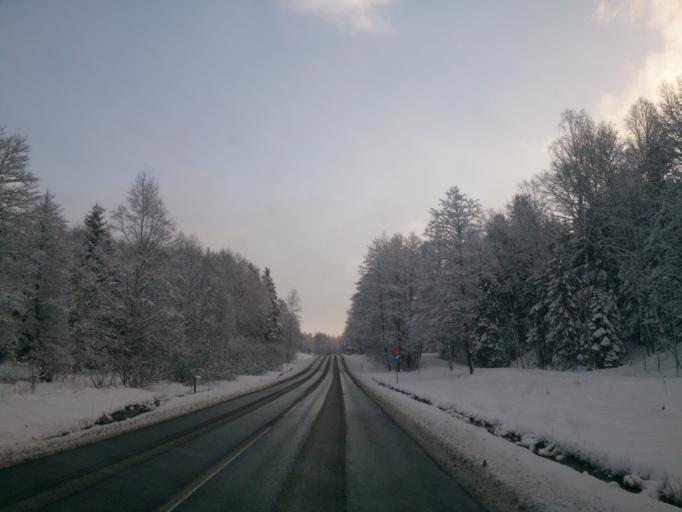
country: SE
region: Stockholm
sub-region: Varmdo Kommun
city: Hemmesta
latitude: 59.3035
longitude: 18.4978
